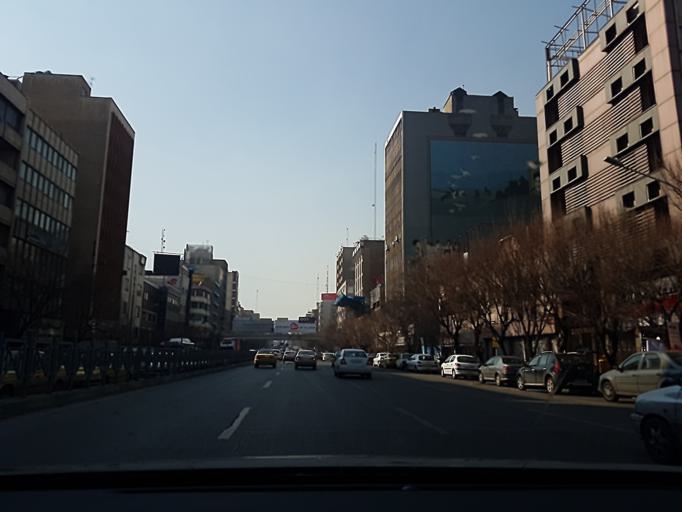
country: IR
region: Tehran
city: Tehran
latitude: 35.7154
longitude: 51.4233
